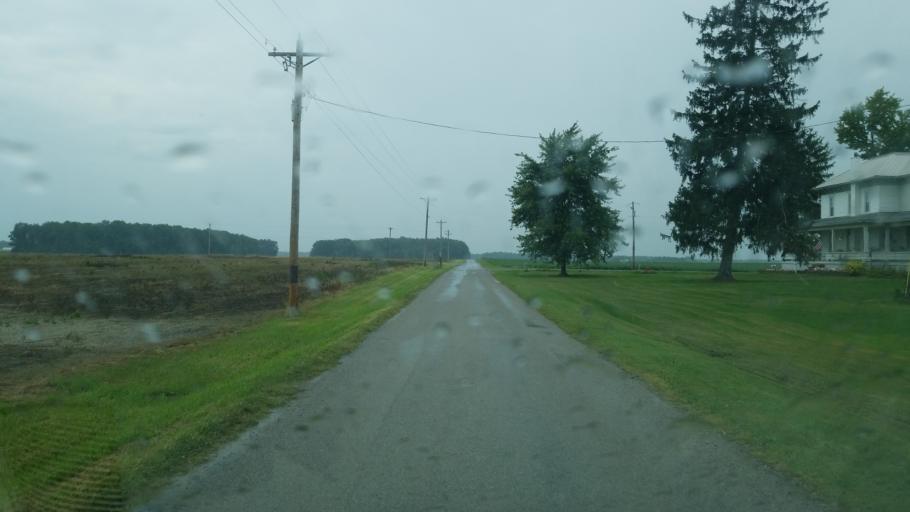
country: US
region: Ohio
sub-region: Huron County
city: Willard
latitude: 41.0107
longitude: -82.8115
